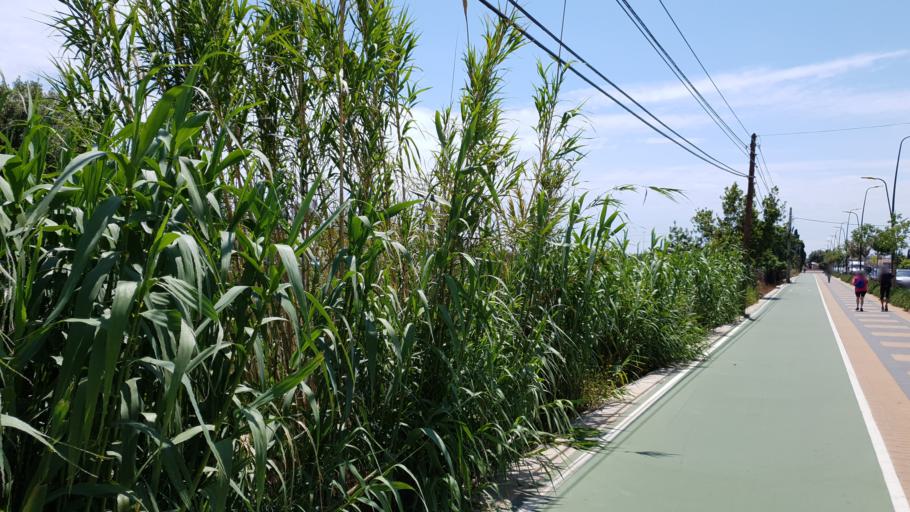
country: ES
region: Valencia
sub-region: Provincia de Castello
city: Burriana
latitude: 39.8800
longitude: -0.0789
